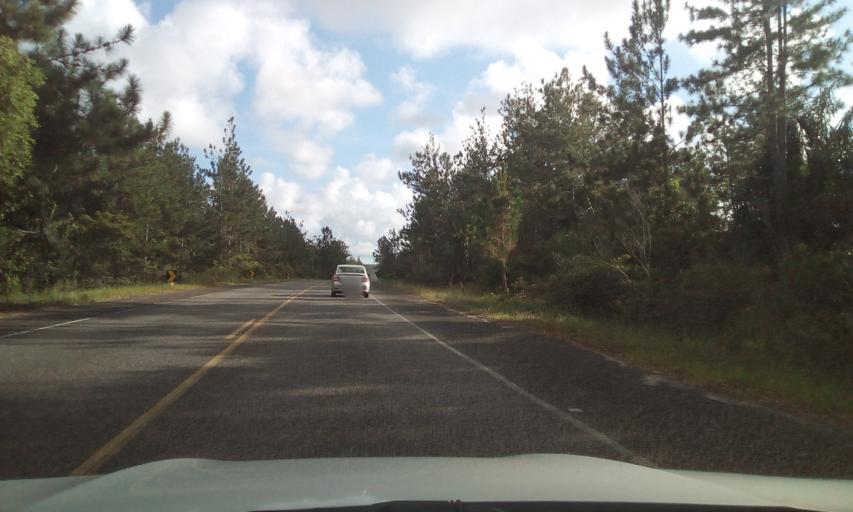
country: BR
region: Bahia
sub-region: Entre Rios
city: Entre Rios
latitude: -12.1524
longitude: -37.8013
